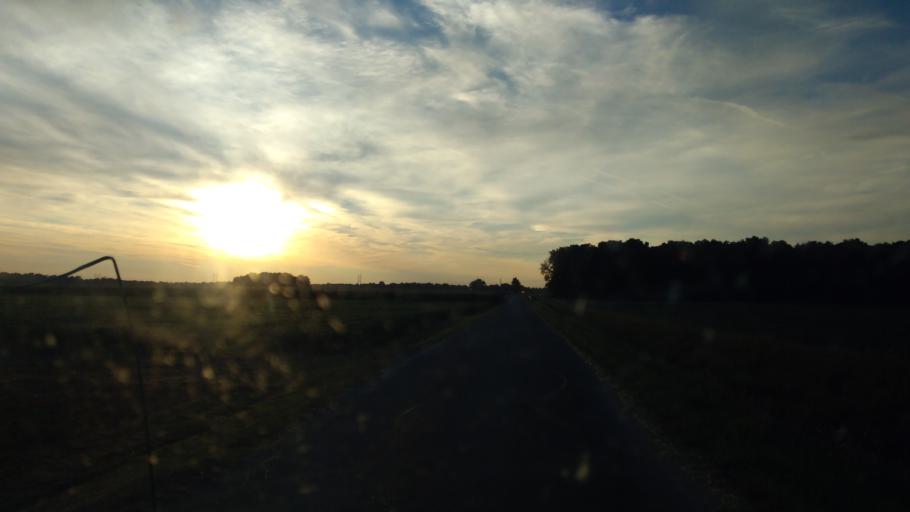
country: US
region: Indiana
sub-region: Adams County
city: Berne
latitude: 40.6413
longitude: -85.0577
